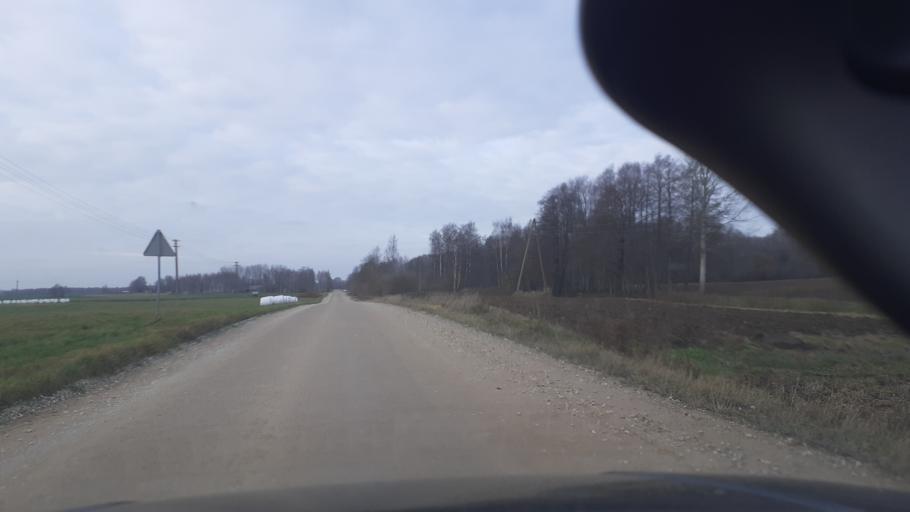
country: LV
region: Alsunga
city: Alsunga
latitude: 56.9137
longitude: 21.6546
